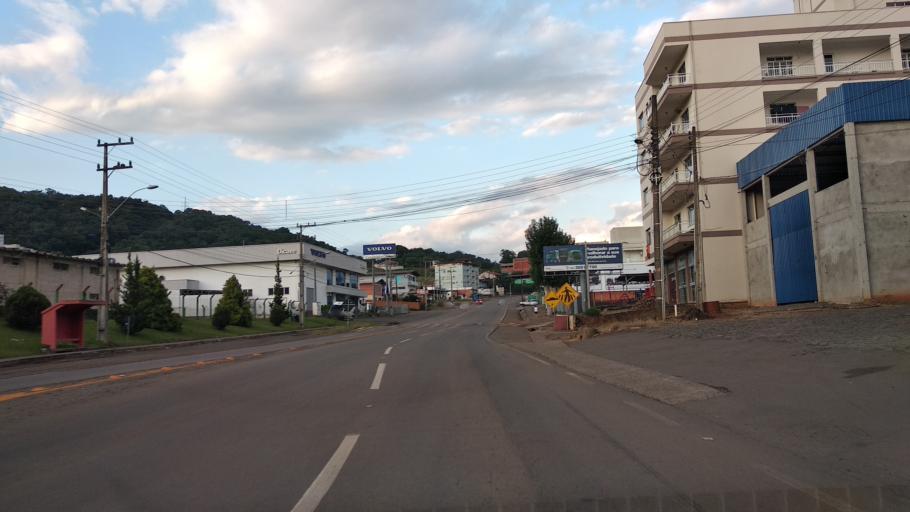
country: BR
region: Santa Catarina
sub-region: Videira
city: Videira
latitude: -27.0002
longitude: -51.1208
